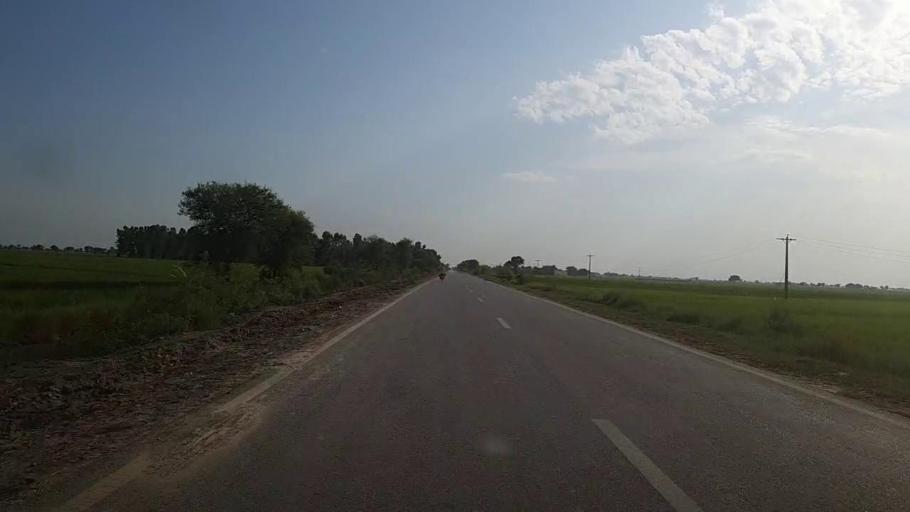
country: PK
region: Sindh
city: Thul
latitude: 28.2238
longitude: 68.7608
